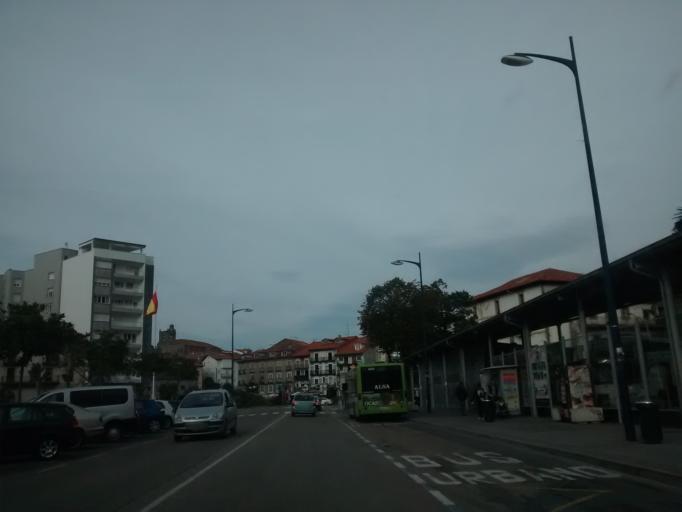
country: ES
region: Cantabria
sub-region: Provincia de Cantabria
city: Laredo
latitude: 43.4095
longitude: -3.4135
